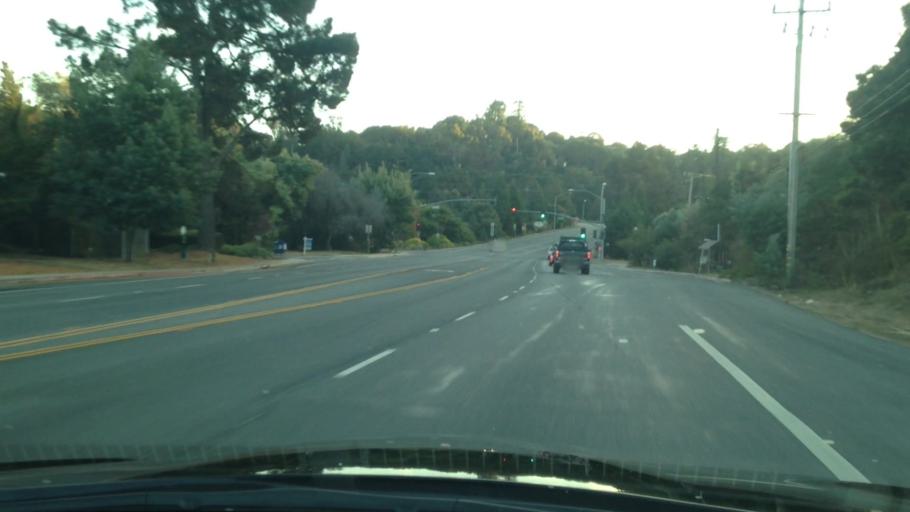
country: US
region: California
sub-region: Santa Cruz County
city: Aptos
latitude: 36.9732
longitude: -121.8710
